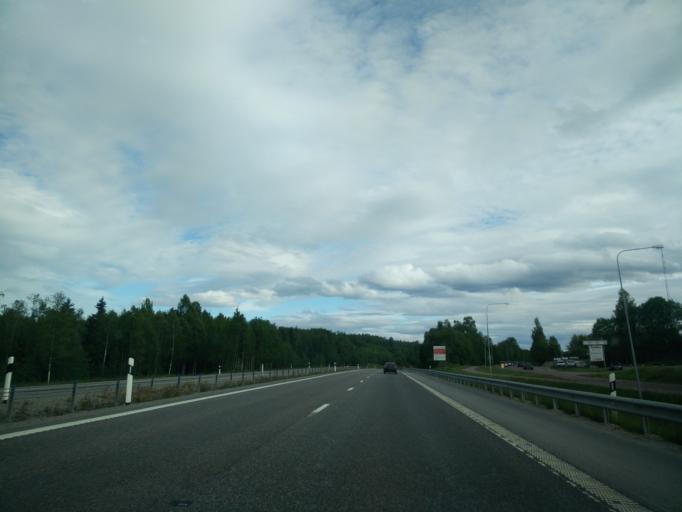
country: SE
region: Vaesternorrland
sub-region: Sundsvalls Kommun
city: Johannedal
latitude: 62.4303
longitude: 17.3455
